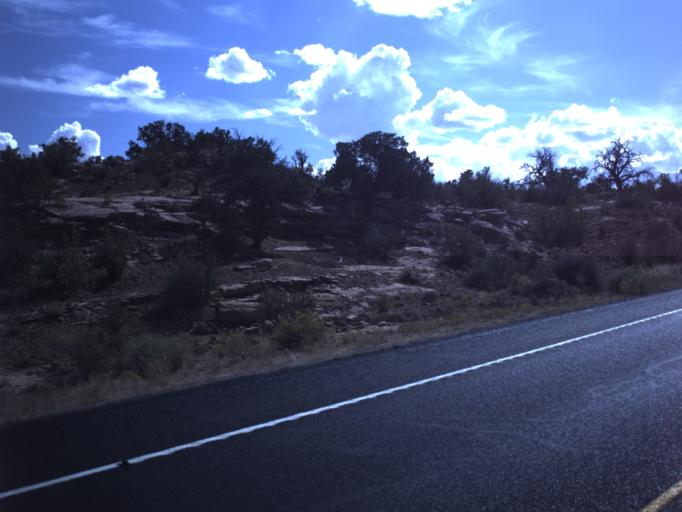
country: US
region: Utah
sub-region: Grand County
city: Moab
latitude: 38.6324
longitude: -109.7966
